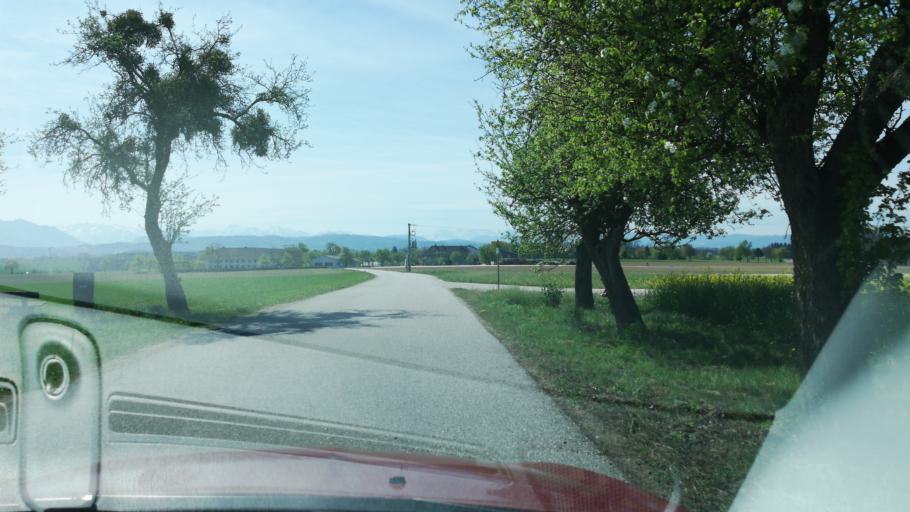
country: AT
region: Upper Austria
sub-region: Politischer Bezirk Steyr-Land
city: Pfarrkirchen bei Bad Hall
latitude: 48.0397
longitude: 14.1858
